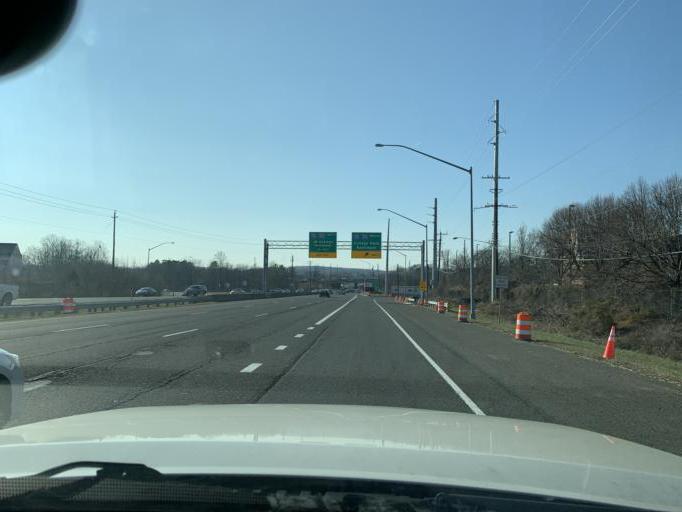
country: US
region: Maryland
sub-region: Prince George's County
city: Largo
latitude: 38.8939
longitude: -76.8420
